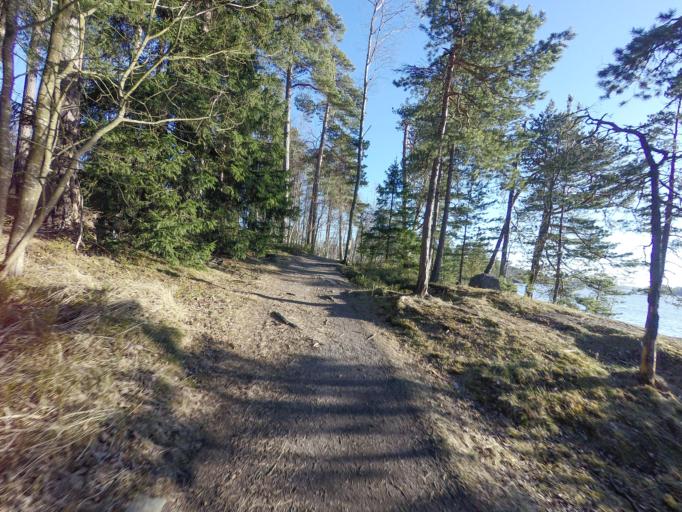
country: FI
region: Uusimaa
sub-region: Helsinki
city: Helsinki
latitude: 60.1828
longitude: 25.0344
